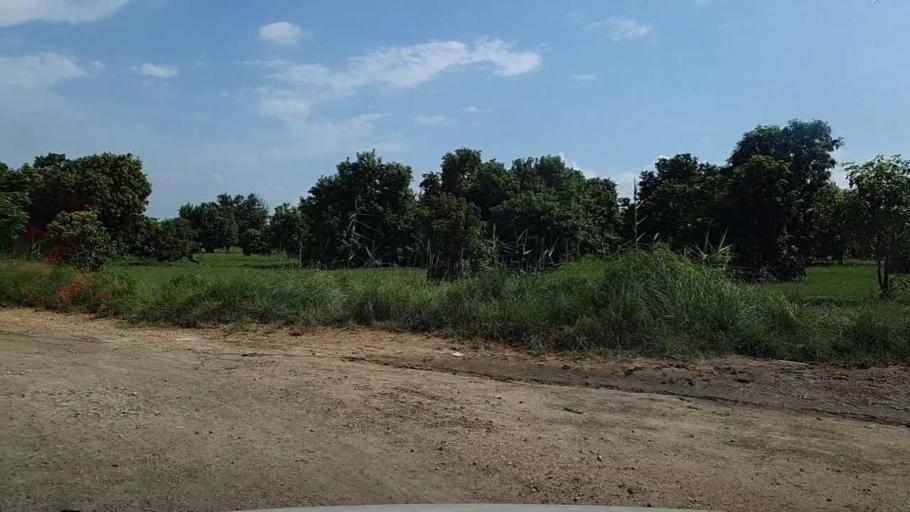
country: PK
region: Sindh
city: Bhiria
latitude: 26.9107
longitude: 68.2242
